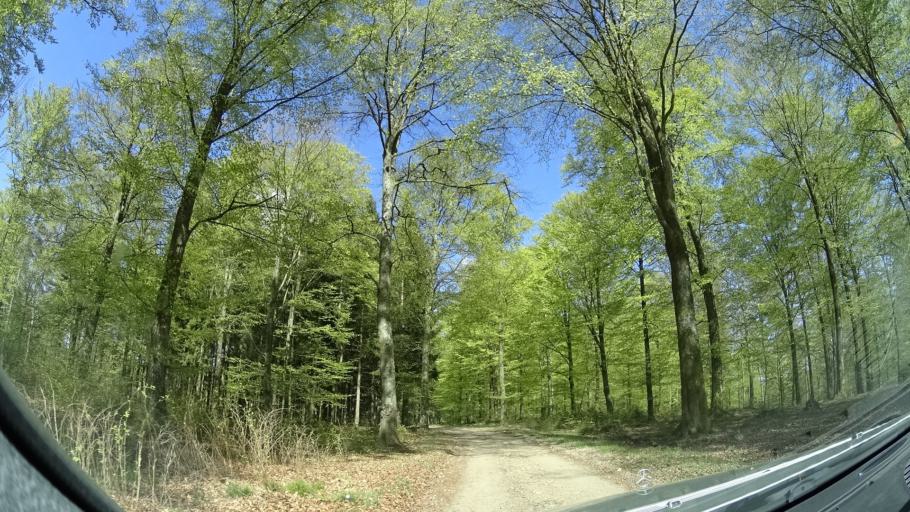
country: SE
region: Skane
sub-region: Hassleholms Kommun
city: Tormestorp
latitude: 56.0986
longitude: 13.6962
